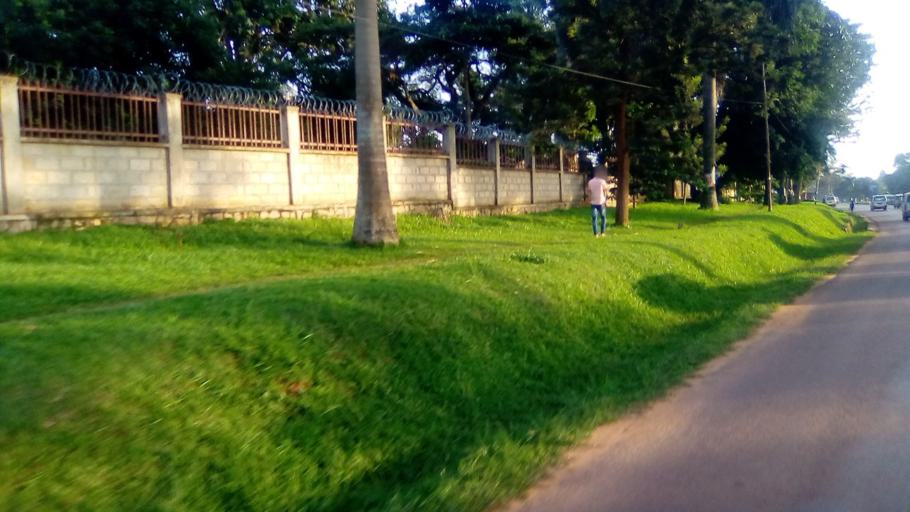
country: UG
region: Central Region
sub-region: Wakiso District
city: Kajansi
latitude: 0.1224
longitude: 32.5293
